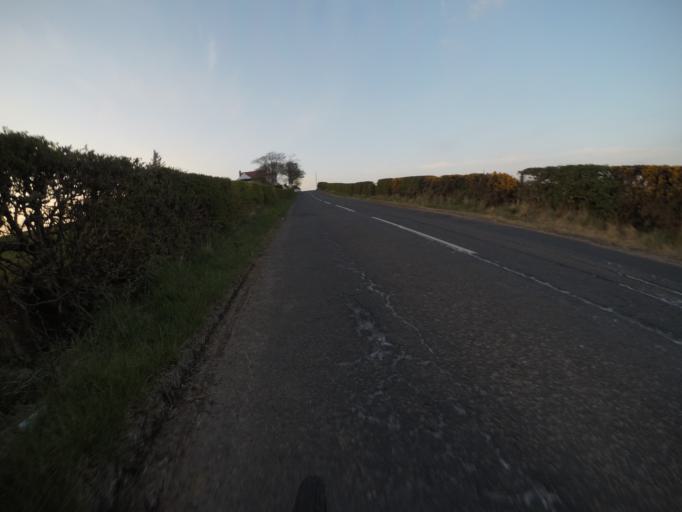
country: GB
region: Scotland
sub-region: South Ayrshire
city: Dundonald
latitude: 55.5534
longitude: -4.6185
